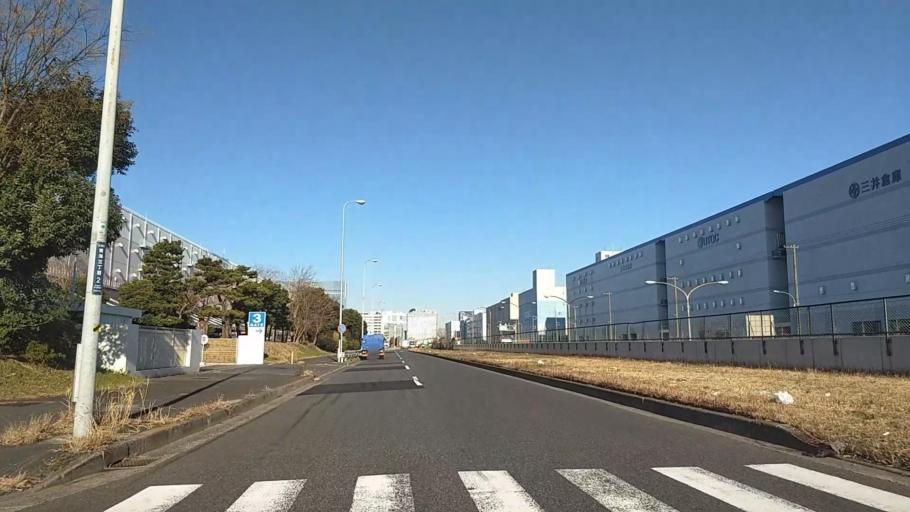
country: JP
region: Kanagawa
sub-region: Kawasaki-shi
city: Kawasaki
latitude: 35.6095
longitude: 139.7880
